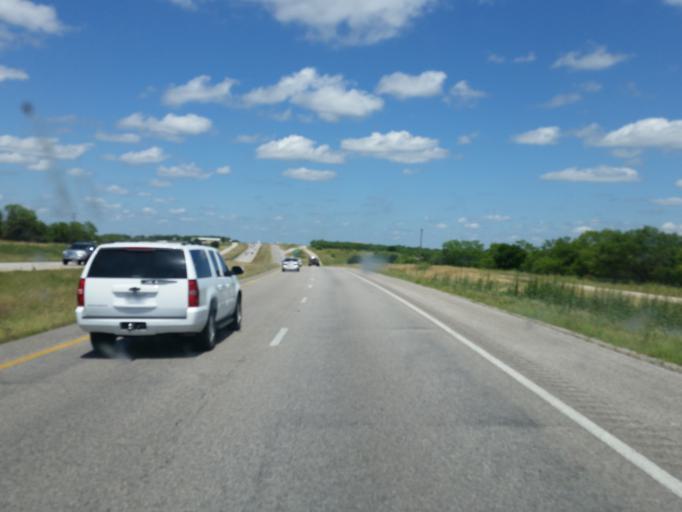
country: US
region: Texas
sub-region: Eastland County
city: Cisco
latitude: 32.3723
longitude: -99.1858
